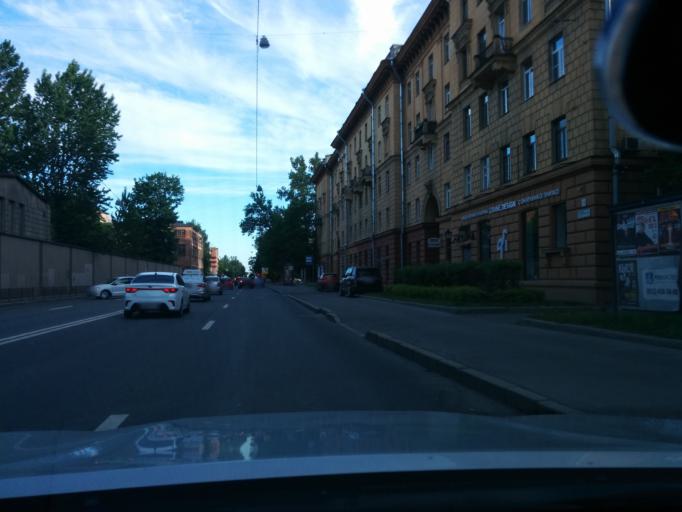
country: RU
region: Leningrad
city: Sampsonievskiy
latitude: 59.9818
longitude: 30.3362
